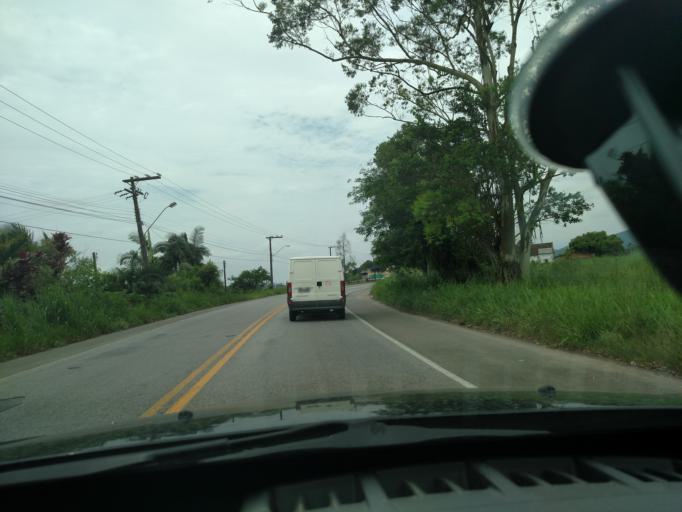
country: BR
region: Santa Catarina
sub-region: Itajai
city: Itajai
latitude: -26.8741
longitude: -48.7885
